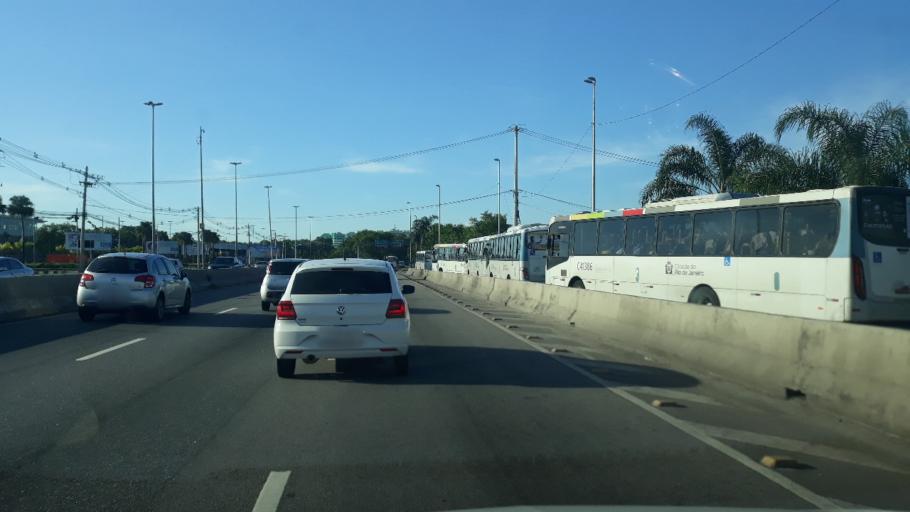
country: BR
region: Rio de Janeiro
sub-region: Sao Joao De Meriti
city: Sao Joao de Meriti
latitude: -22.9634
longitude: -43.3573
